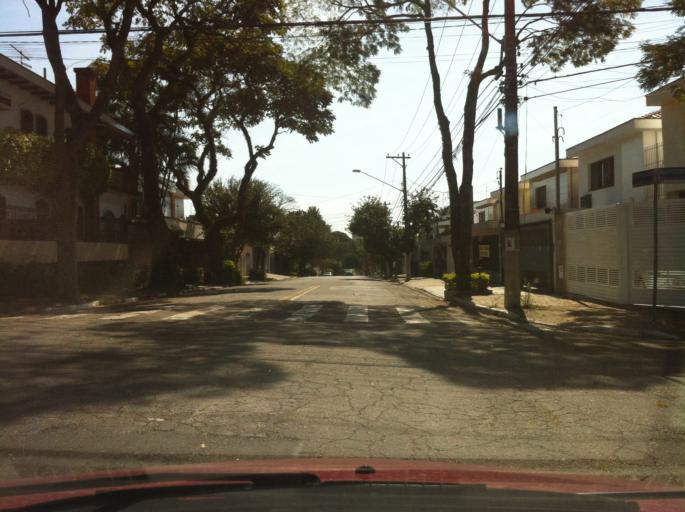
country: BR
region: Sao Paulo
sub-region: Sao Paulo
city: Sao Paulo
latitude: -23.6103
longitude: -46.6491
